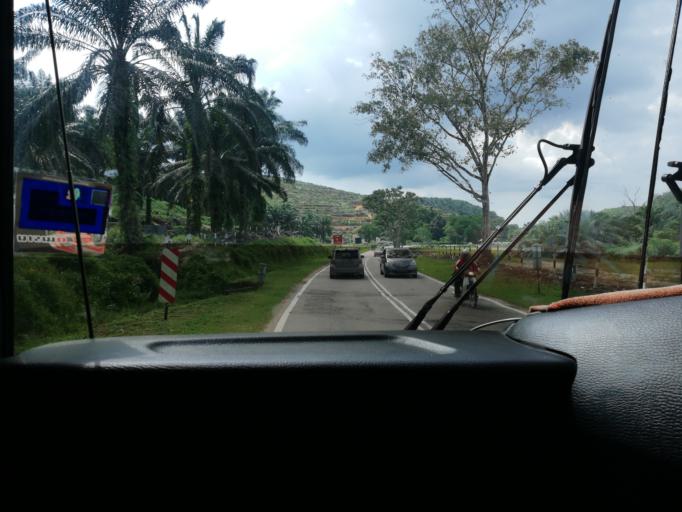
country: MY
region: Kedah
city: Kulim
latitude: 5.3107
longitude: 100.6071
